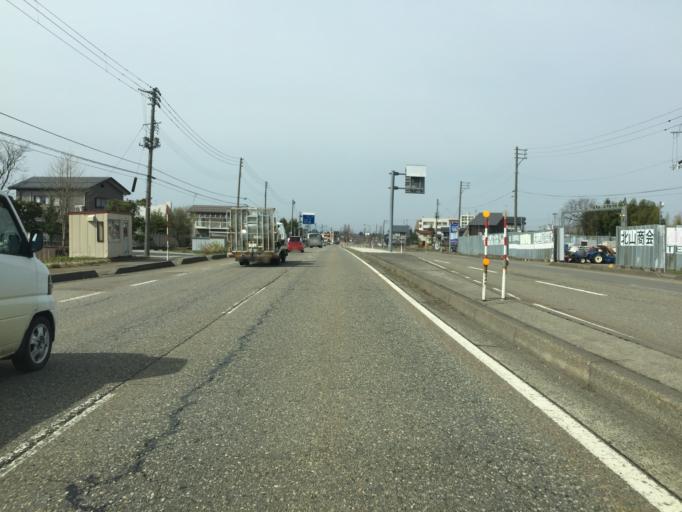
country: JP
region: Niigata
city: Ojiya
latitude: 37.3510
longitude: 138.8291
